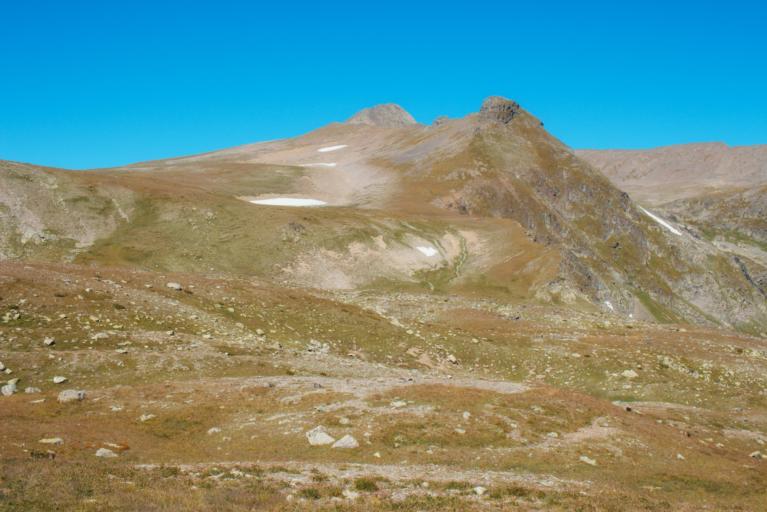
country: RU
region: Karachayevo-Cherkesiya
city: Mednogorskiy
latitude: 43.6167
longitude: 41.1137
